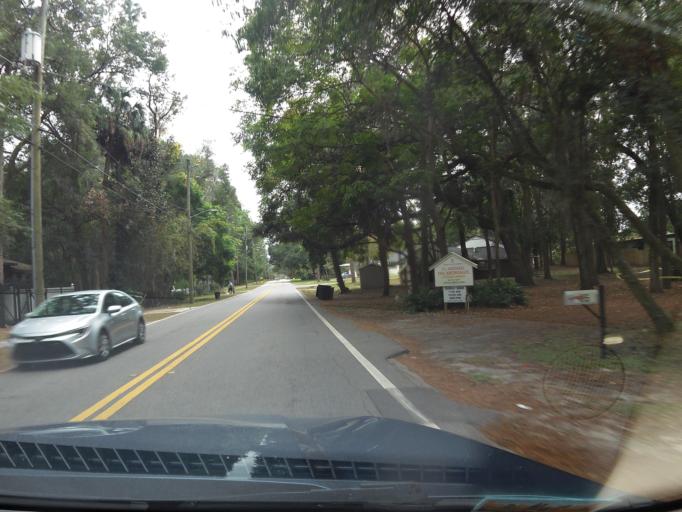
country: US
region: Florida
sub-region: Duval County
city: Jacksonville
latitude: 30.3072
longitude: -81.6029
